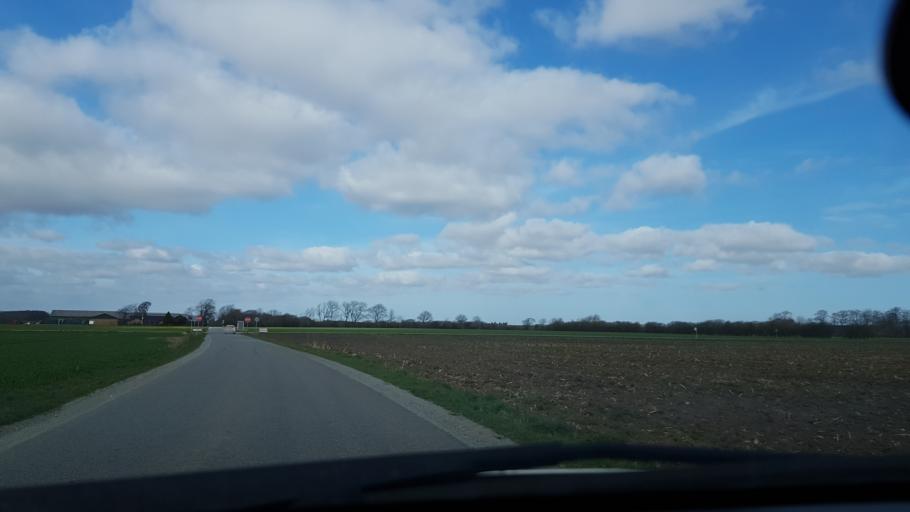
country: DK
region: South Denmark
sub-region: Vejen Kommune
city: Rodding
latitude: 55.3951
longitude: 9.0105
